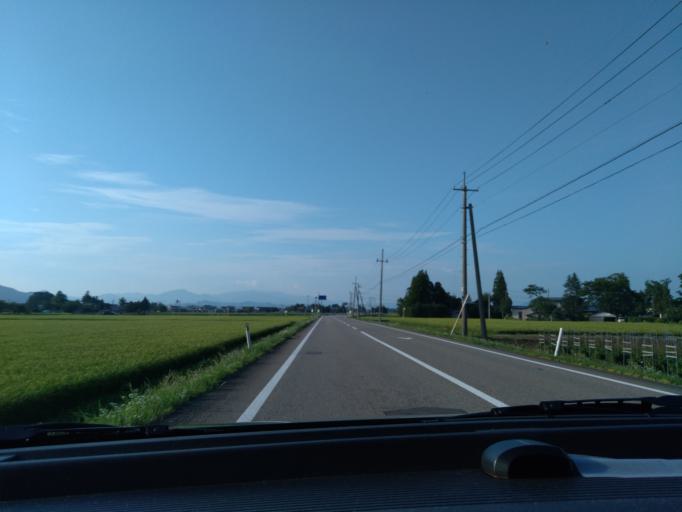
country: JP
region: Akita
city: Kakunodatemachi
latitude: 39.5143
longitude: 140.5586
